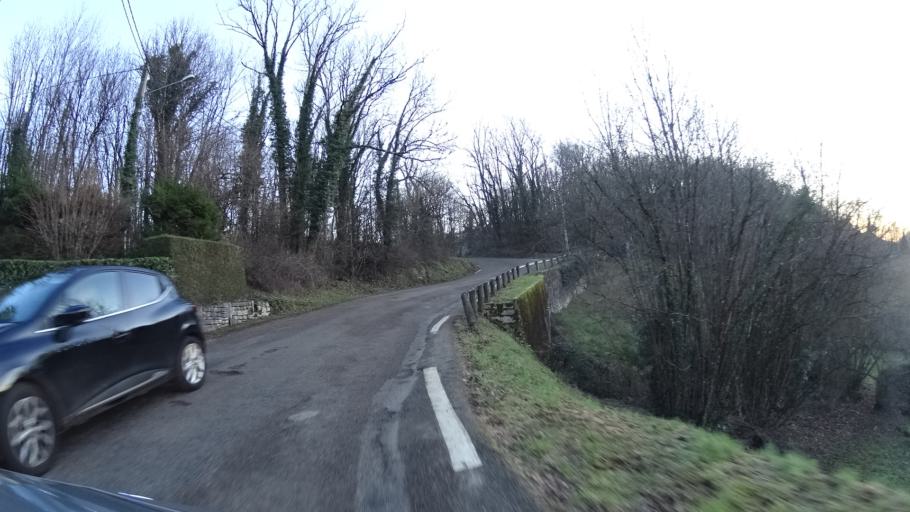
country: FR
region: Franche-Comte
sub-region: Departement du Doubs
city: Besancon
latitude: 47.2248
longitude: 6.0362
